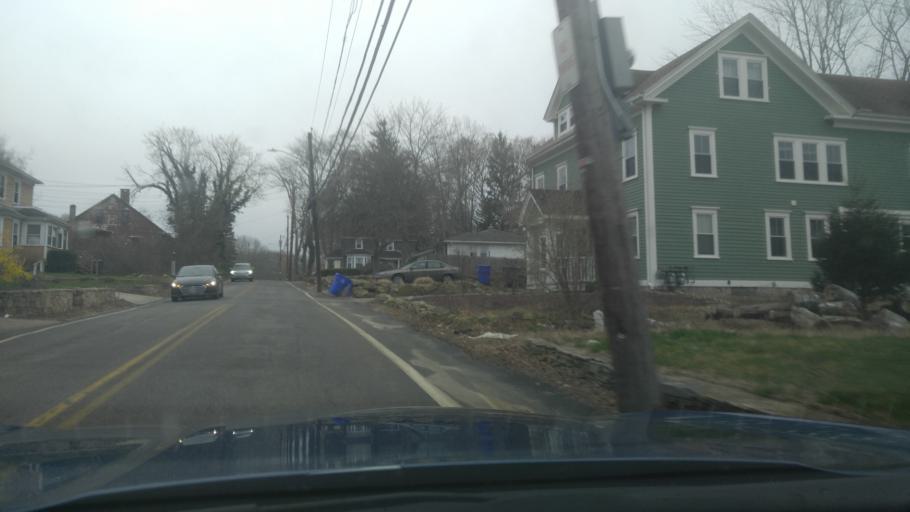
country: US
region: Rhode Island
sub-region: Kent County
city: West Warwick
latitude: 41.6823
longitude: -71.5231
